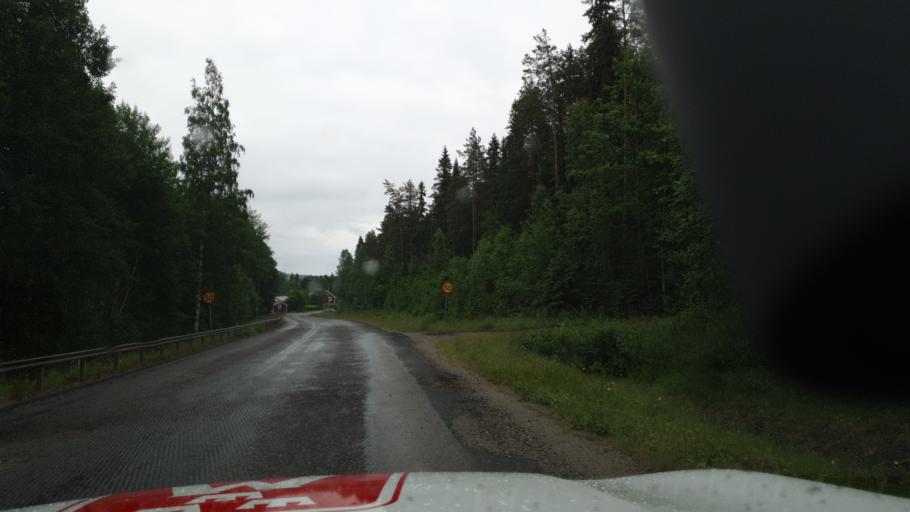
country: SE
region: Vaesterbotten
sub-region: Vannas Kommun
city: Vaennaes
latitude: 63.7865
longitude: 19.8323
